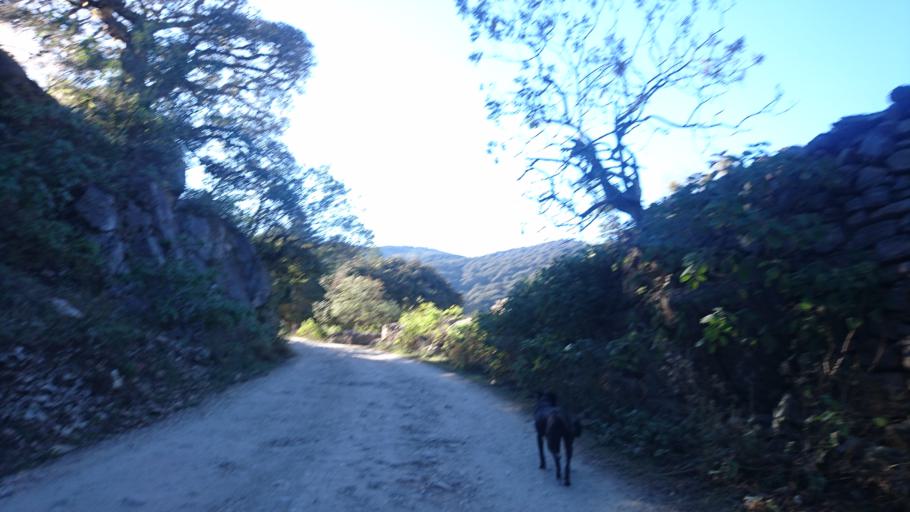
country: MX
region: San Luis Potosi
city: Zaragoza
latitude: 22.0312
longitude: -100.6099
